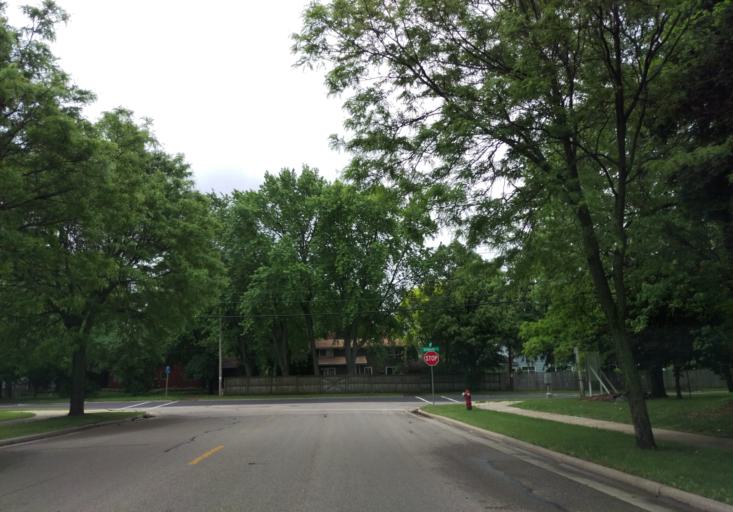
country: US
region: Wisconsin
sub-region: Dane County
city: Middleton
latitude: 43.0468
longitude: -89.4914
